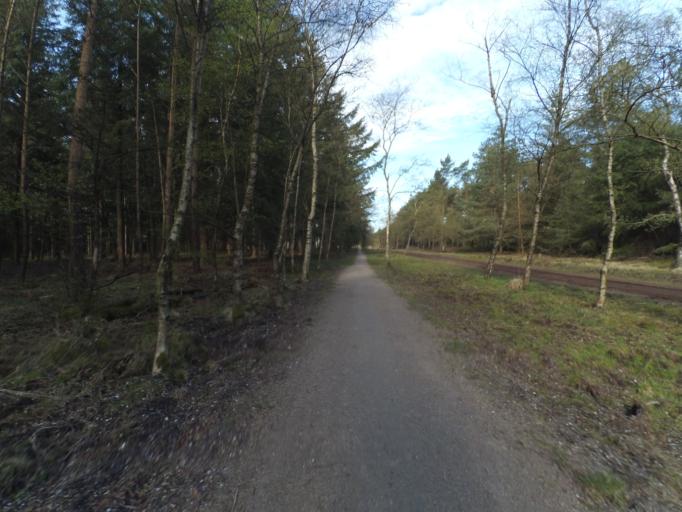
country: NL
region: Gelderland
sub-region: Gemeente Apeldoorn
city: Uddel
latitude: 52.3051
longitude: 5.7684
